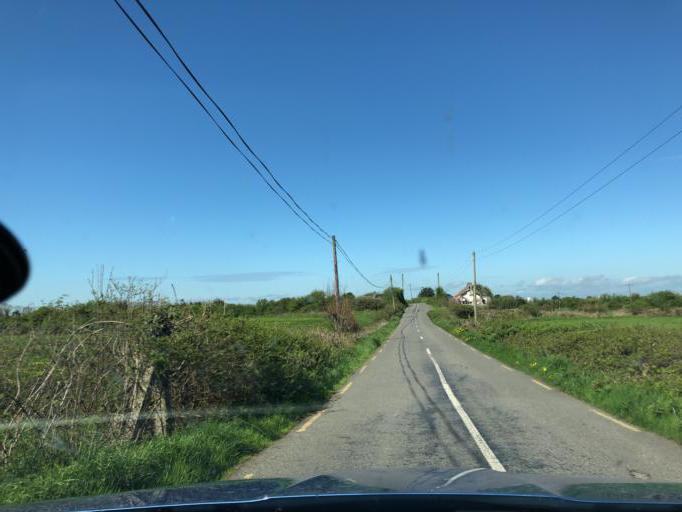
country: IE
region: Connaught
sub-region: County Galway
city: Portumna
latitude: 53.1607
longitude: -8.2668
